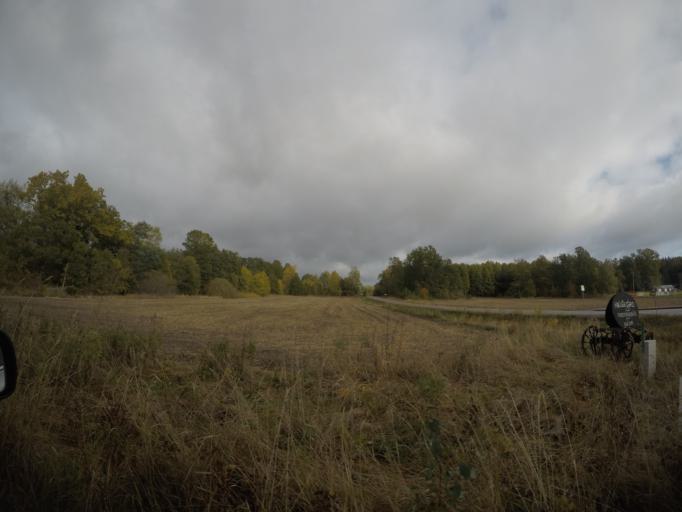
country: SE
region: Soedermanland
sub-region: Eskilstuna Kommun
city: Kvicksund
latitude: 59.3171
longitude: 16.2837
